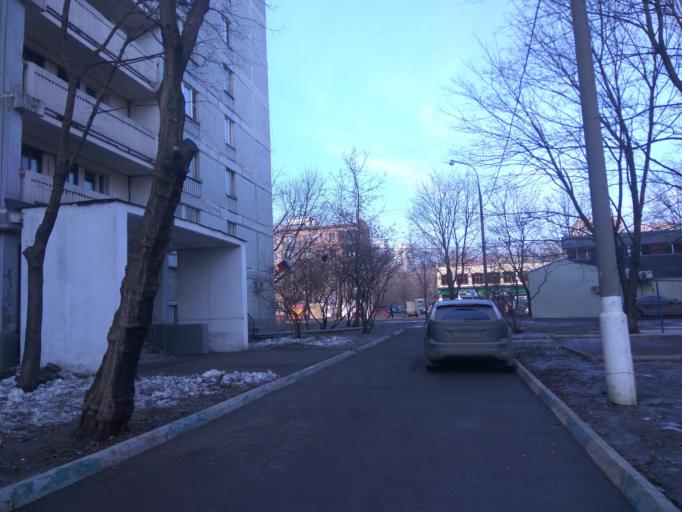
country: RU
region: Moscow
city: Kolomenskoye
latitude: 55.6821
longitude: 37.6814
